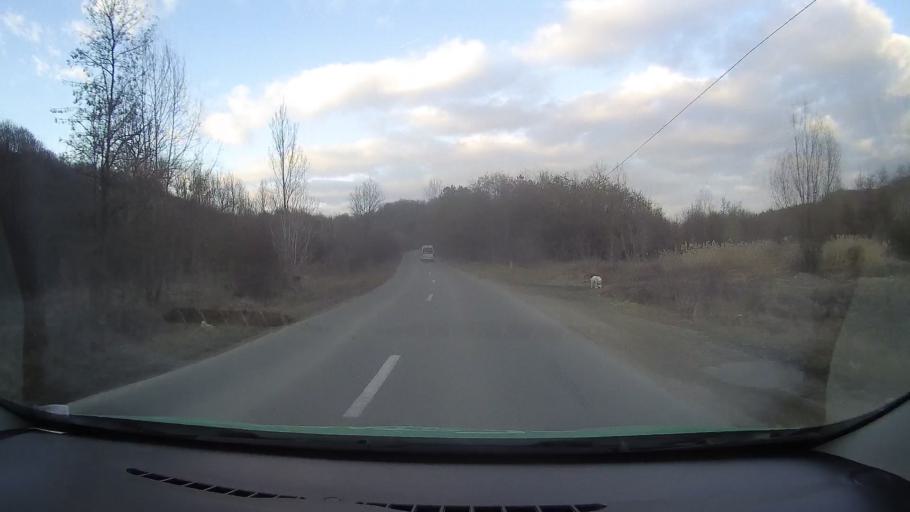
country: RO
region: Dambovita
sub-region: Comuna Gura Ocnitei
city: Gura Ocnitei
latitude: 44.9528
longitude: 25.5963
